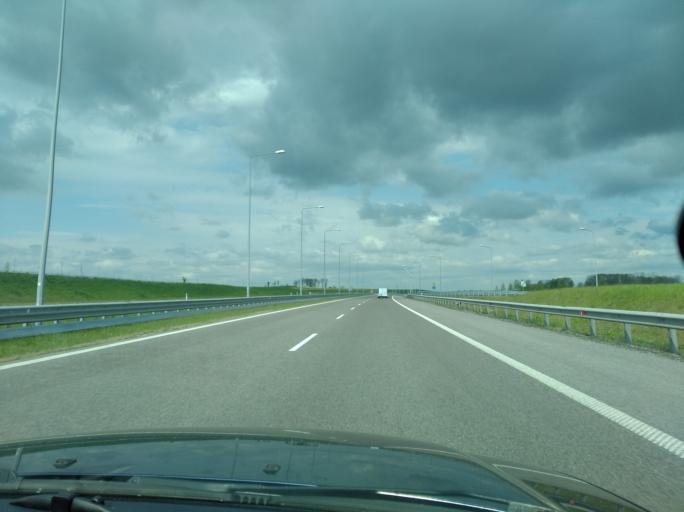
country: PL
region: Subcarpathian Voivodeship
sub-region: Powiat jaroslawski
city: Ostrow
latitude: 49.9174
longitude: 22.7532
